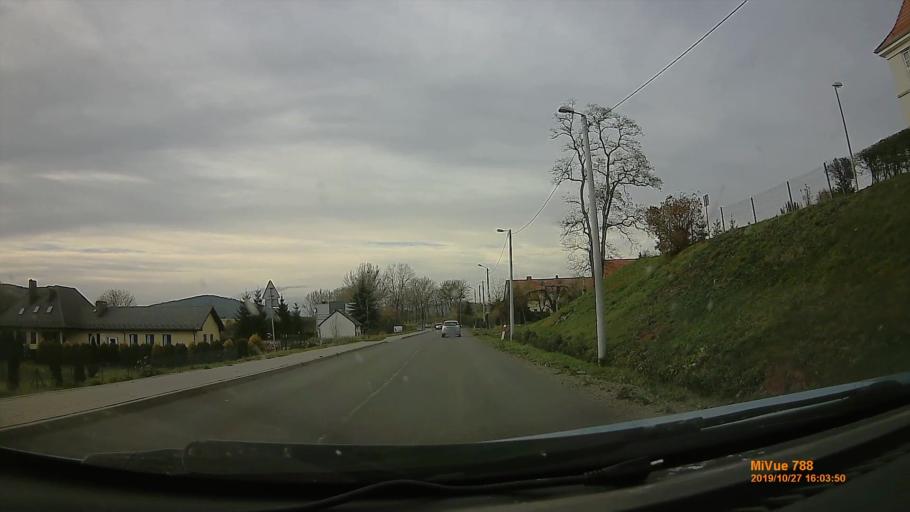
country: PL
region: Lower Silesian Voivodeship
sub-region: Powiat klodzki
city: Nowa Ruda
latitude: 50.5227
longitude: 16.4942
